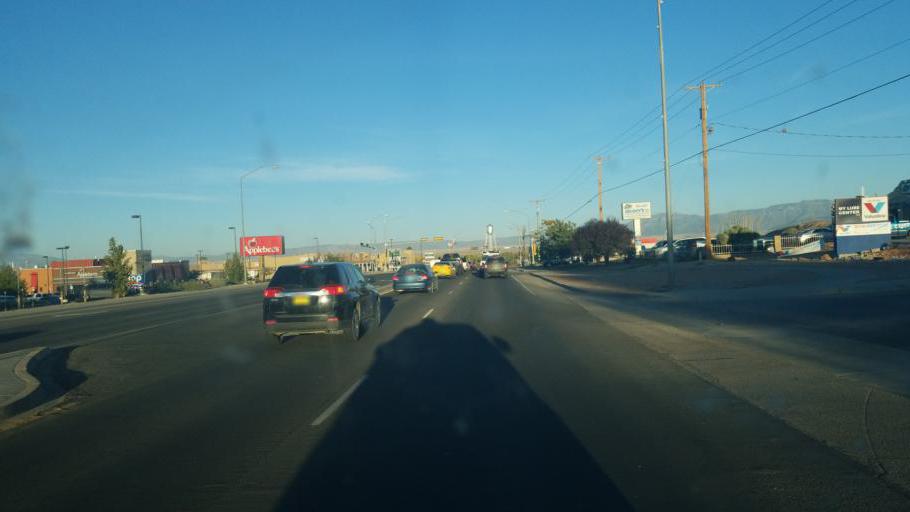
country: US
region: New Mexico
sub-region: Valencia County
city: Los Lunas
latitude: 34.8143
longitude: -106.7522
